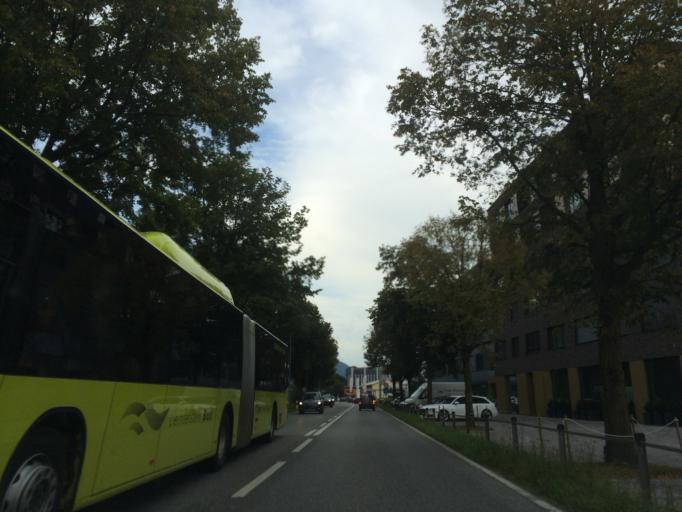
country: CH
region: Saint Gallen
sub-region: Wahlkreis Werdenberg
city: Haag (Rheintal)
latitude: 47.2048
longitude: 9.5017
